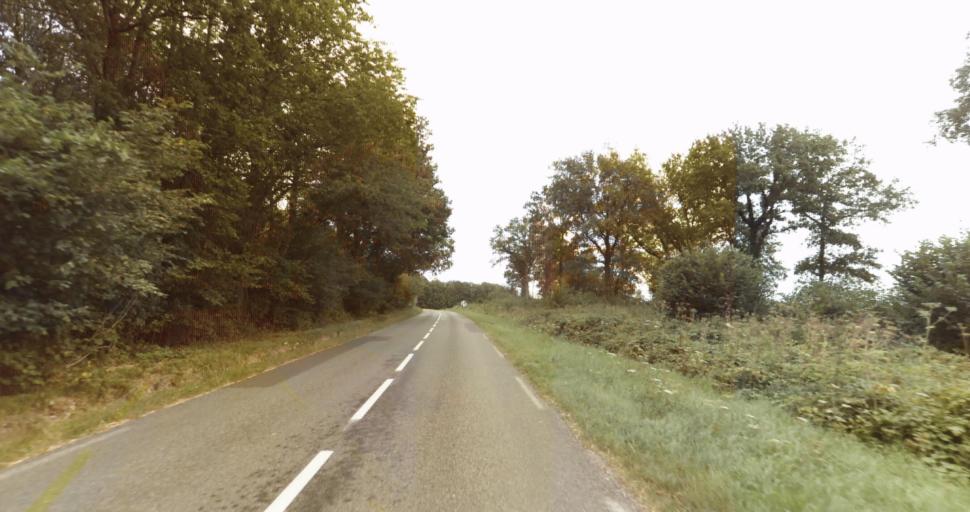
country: FR
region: Haute-Normandie
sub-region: Departement de l'Eure
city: Menilles
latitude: 48.9818
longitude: 1.2679
